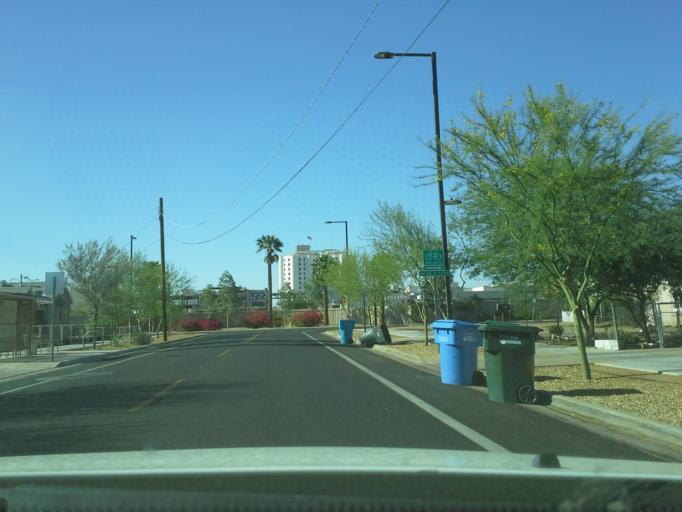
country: US
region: Arizona
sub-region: Maricopa County
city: Phoenix
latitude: 33.4606
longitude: -112.0589
